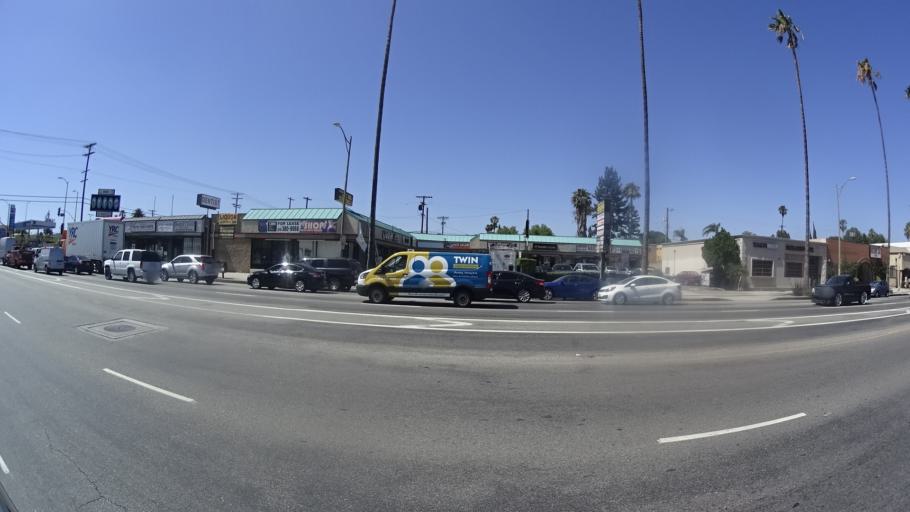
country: US
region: California
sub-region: Los Angeles County
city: Van Nuys
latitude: 34.2013
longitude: -118.4828
